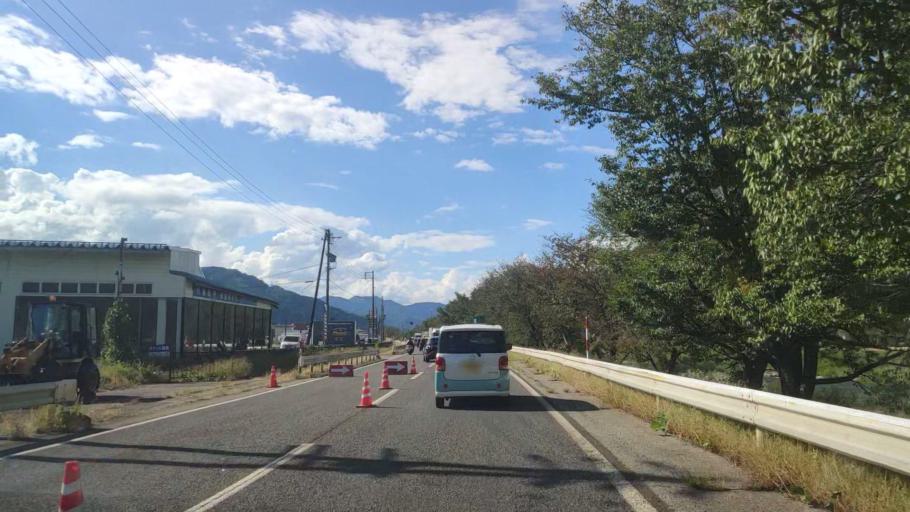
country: JP
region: Gifu
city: Takayama
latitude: 36.2038
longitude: 137.2277
